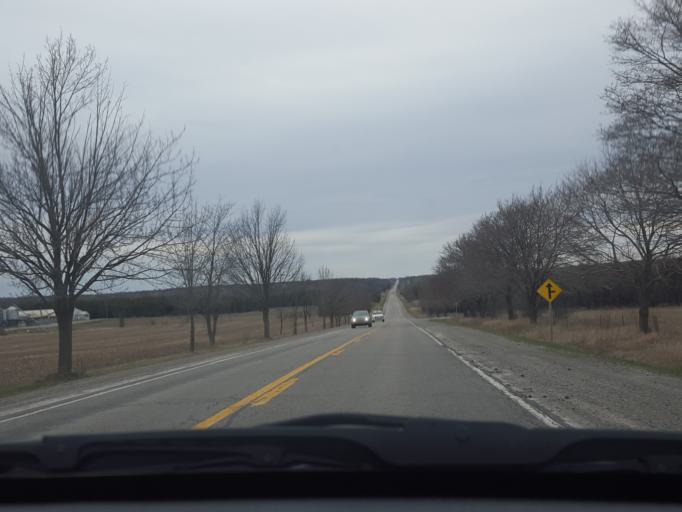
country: CA
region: Ontario
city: Uxbridge
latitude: 44.2805
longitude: -79.1636
